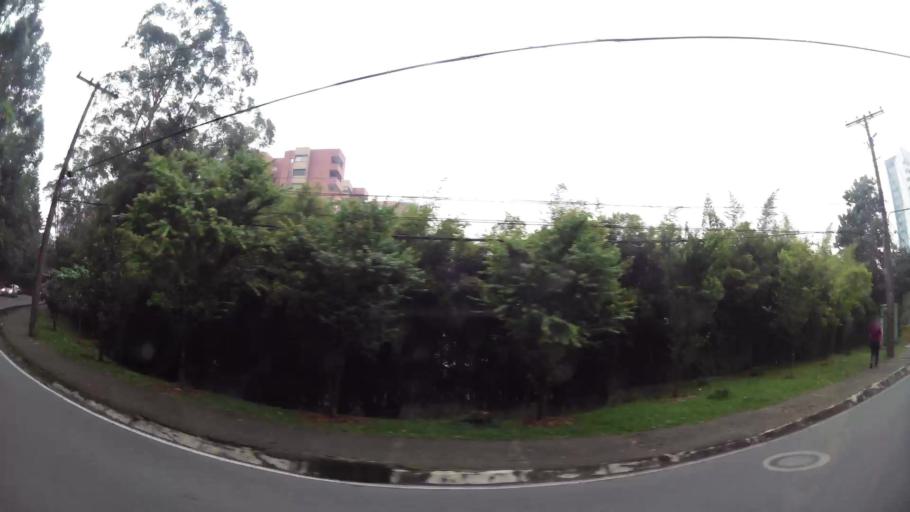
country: CO
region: Antioquia
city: Envigado
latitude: 6.1940
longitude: -75.5591
